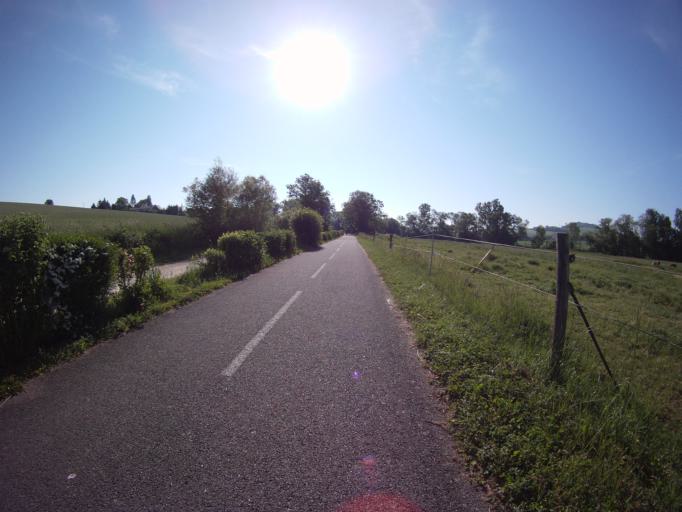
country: FR
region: Lorraine
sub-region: Departement de Meurthe-et-Moselle
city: Eulmont
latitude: 48.7409
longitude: 6.2320
